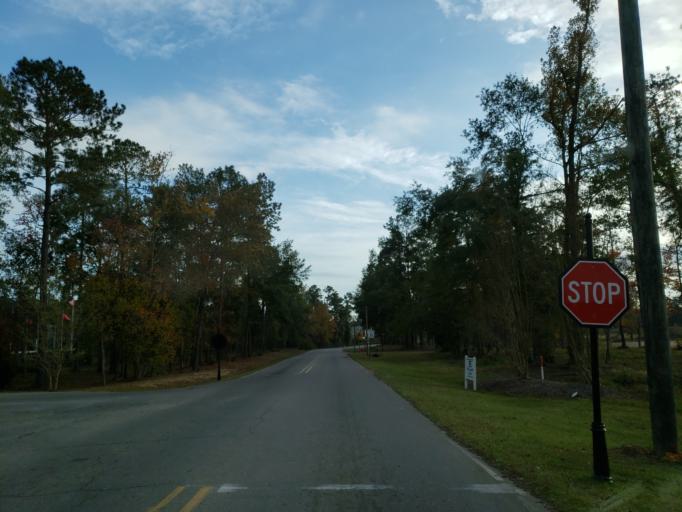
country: US
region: Mississippi
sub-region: Forrest County
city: Hattiesburg
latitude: 31.3030
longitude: -89.2941
